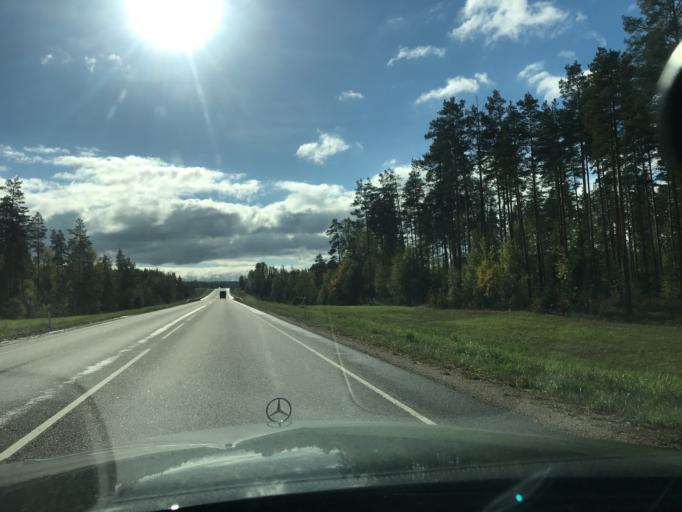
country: EE
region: Vorumaa
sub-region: Voru linn
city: Voru
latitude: 57.8229
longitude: 27.0639
